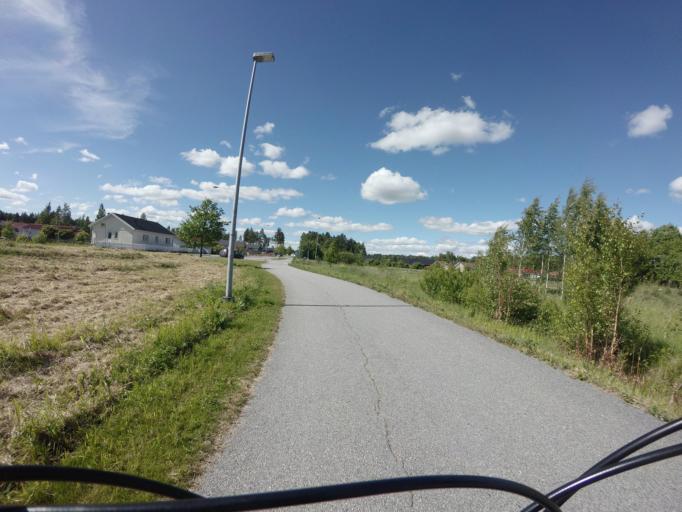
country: FI
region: Varsinais-Suomi
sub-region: Turku
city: Vahto
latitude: 60.5369
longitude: 22.3113
